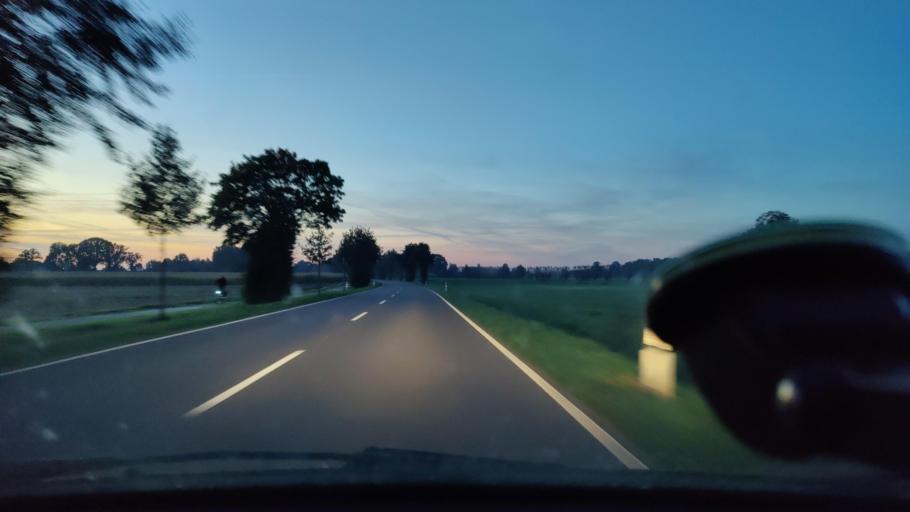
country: DE
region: North Rhine-Westphalia
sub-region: Regierungsbezirk Munster
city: Sudlohn
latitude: 51.8986
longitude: 6.8818
